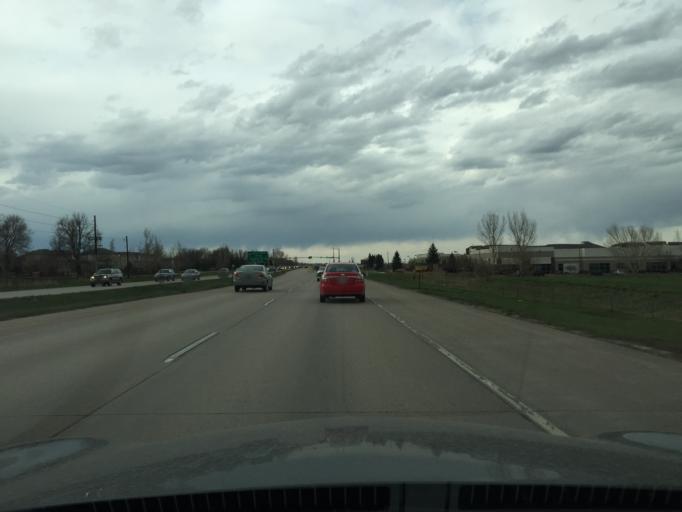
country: US
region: Colorado
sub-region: Boulder County
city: Lafayette
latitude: 39.9640
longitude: -105.0901
